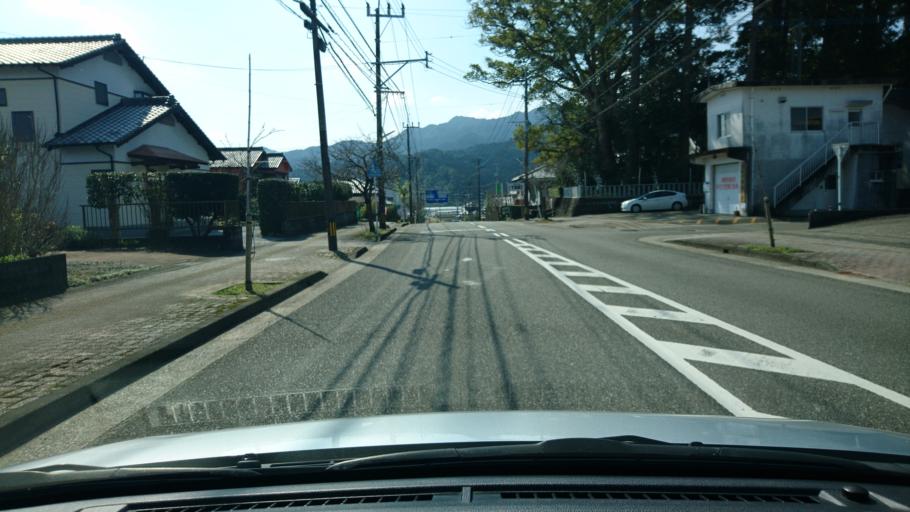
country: JP
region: Miyazaki
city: Miyazaki-shi
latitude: 31.8269
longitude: 131.4201
